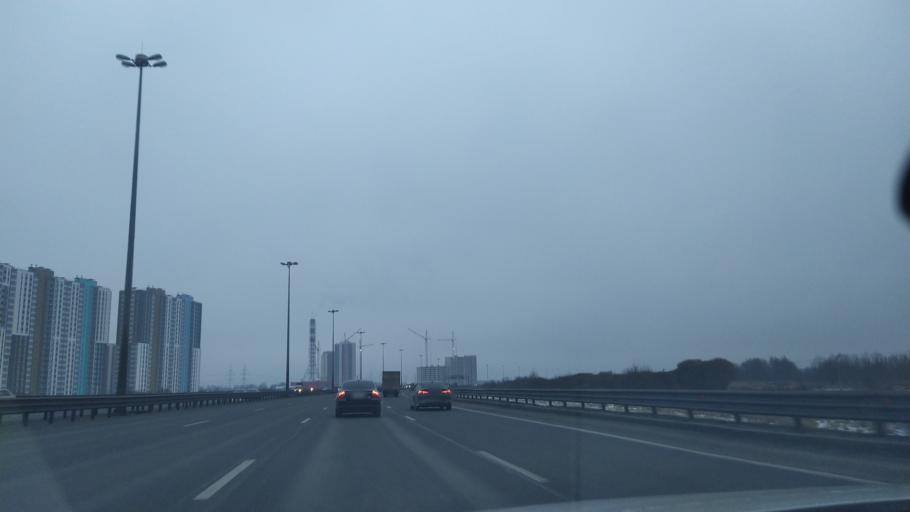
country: RU
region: St.-Petersburg
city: Krasnogvargeisky
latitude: 60.0117
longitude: 30.4728
